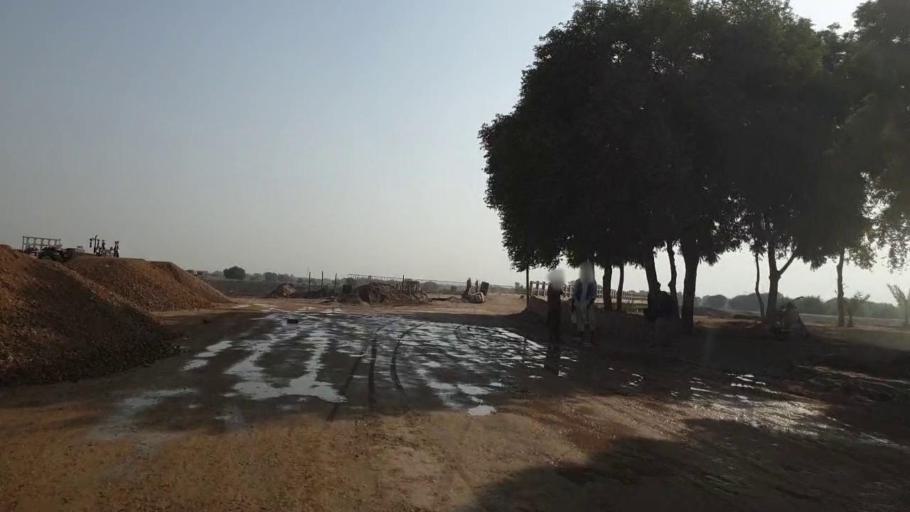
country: PK
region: Sindh
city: Bhan
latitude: 26.5015
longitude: 67.7822
